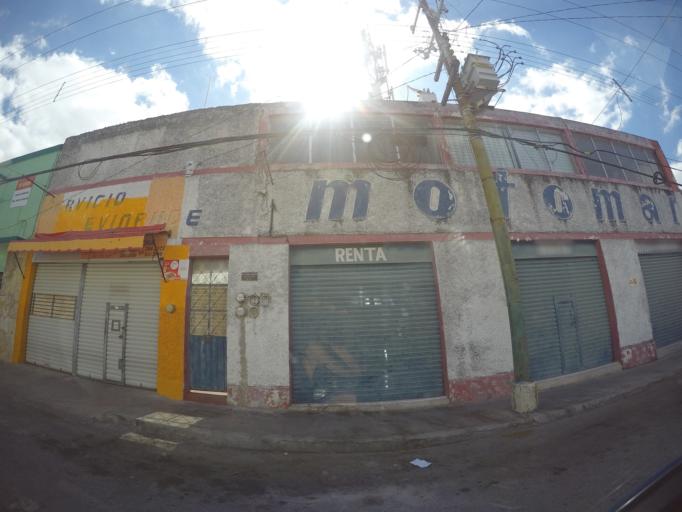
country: MX
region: Yucatan
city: Merida
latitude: 20.9762
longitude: -89.6260
